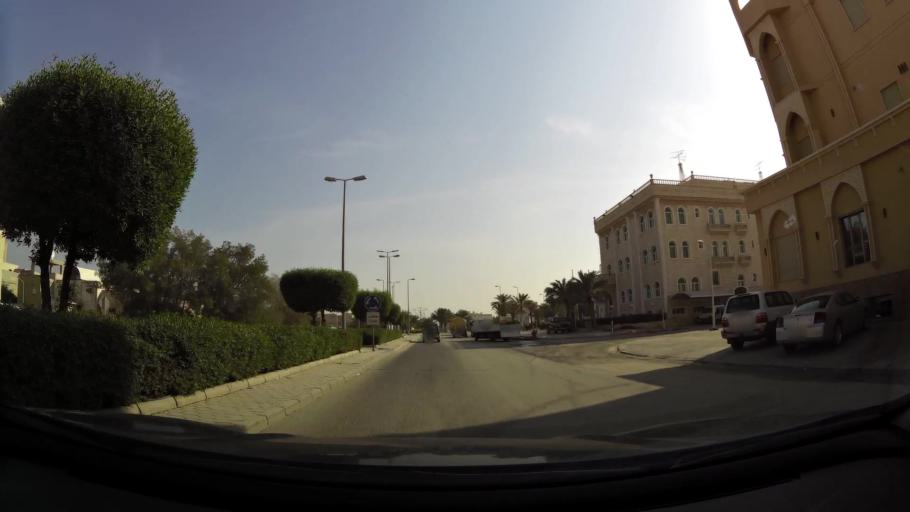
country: KW
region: Al Ahmadi
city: Ar Riqqah
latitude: 29.1448
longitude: 48.1067
